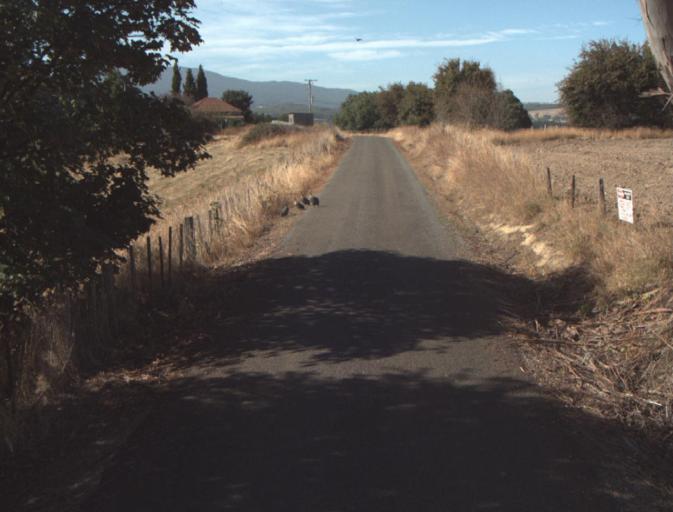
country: AU
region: Tasmania
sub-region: Dorset
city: Bridport
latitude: -41.1678
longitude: 147.2294
